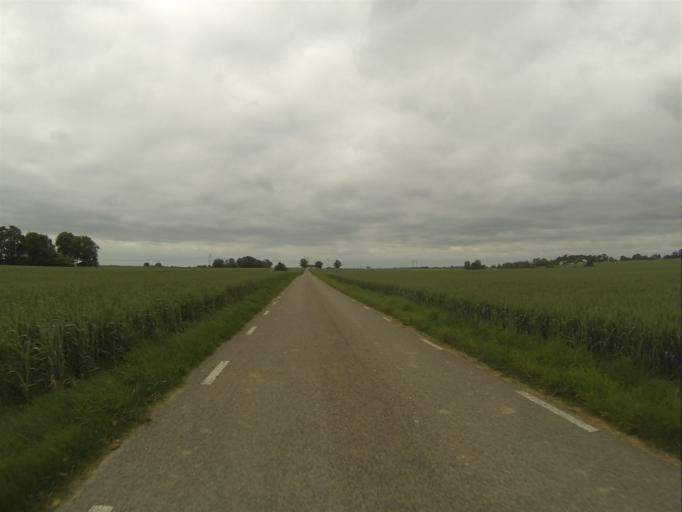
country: SE
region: Skane
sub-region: Staffanstorps Kommun
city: Staffanstorp
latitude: 55.6753
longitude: 13.2464
